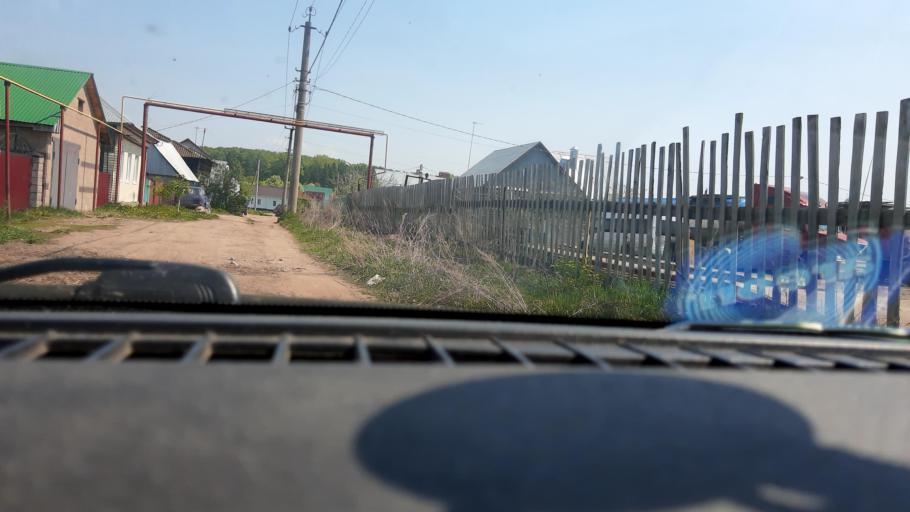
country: RU
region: Bashkortostan
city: Blagoveshchensk
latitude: 55.0224
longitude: 55.9818
